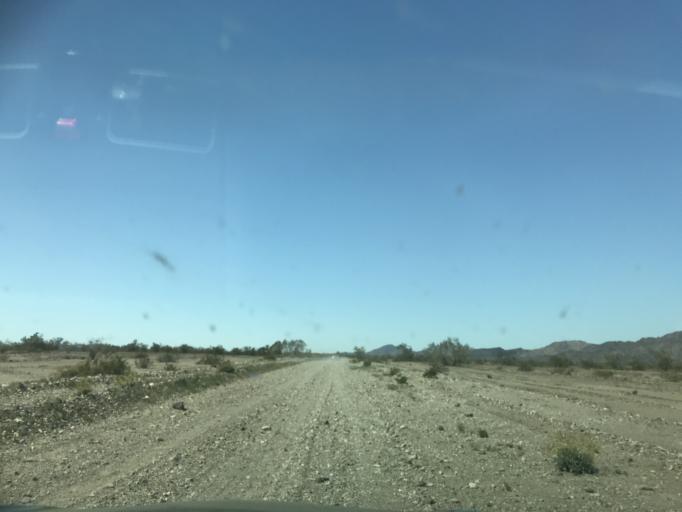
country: US
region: California
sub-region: Riverside County
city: Mesa Verde
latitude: 33.4805
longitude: -114.9297
